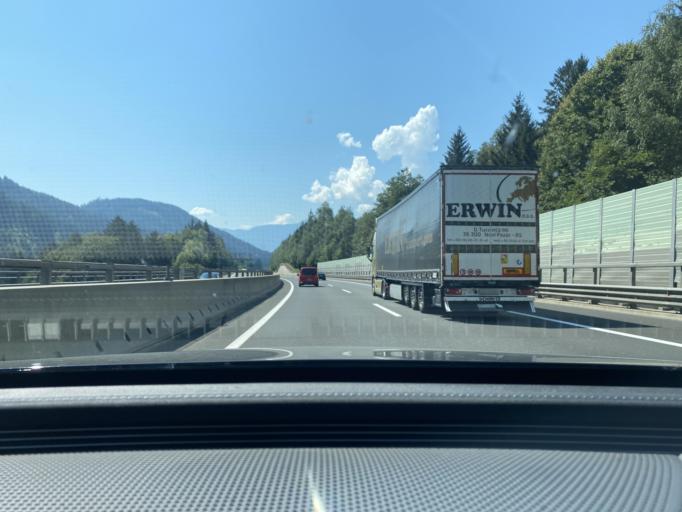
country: AT
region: Carinthia
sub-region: Politischer Bezirk Spittal an der Drau
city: Trebesing
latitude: 46.8769
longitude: 13.5032
